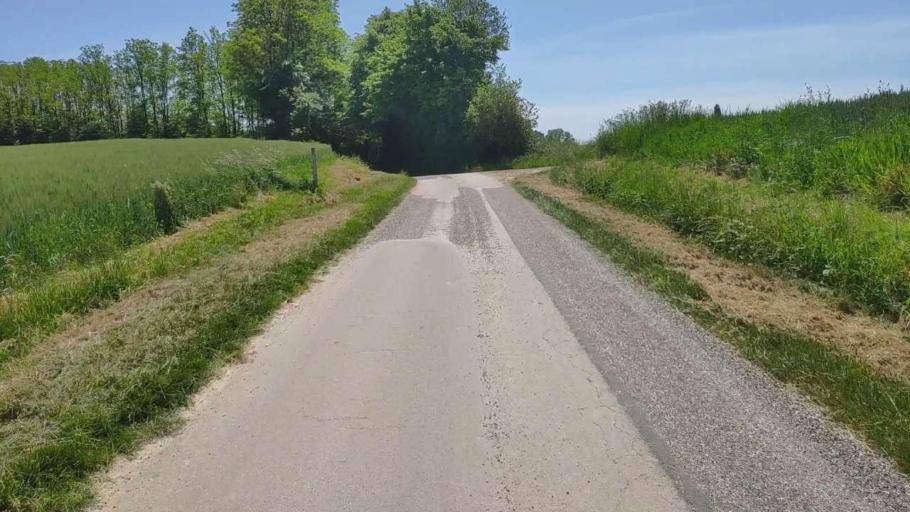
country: FR
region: Franche-Comte
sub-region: Departement du Jura
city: Bletterans
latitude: 46.7566
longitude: 5.4047
